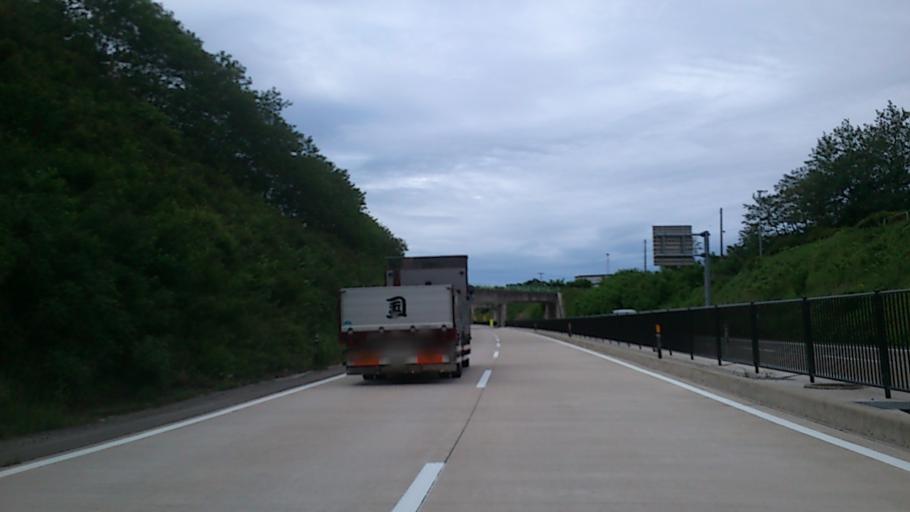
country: JP
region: Akita
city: Akita Shi
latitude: 39.6763
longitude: 140.0719
